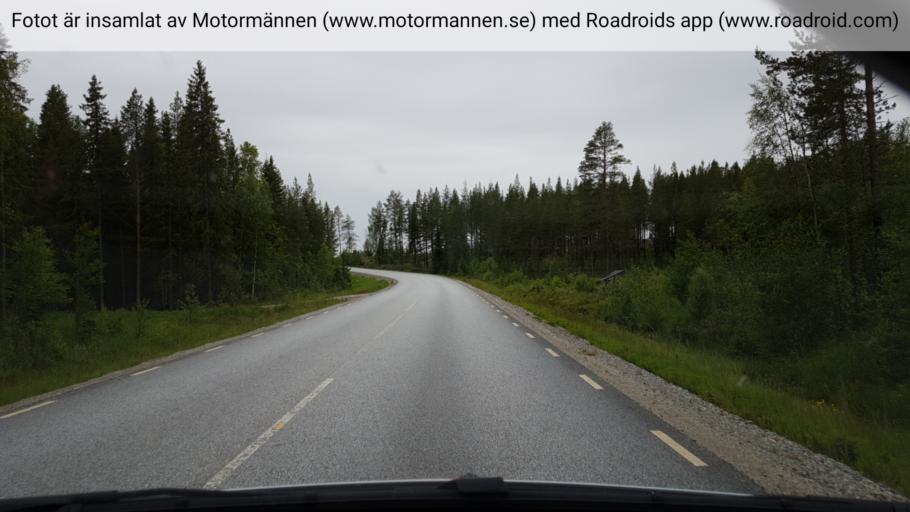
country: SE
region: Vaesterbotten
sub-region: Bjurholms Kommun
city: Bjurholm
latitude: 64.1699
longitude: 19.3908
